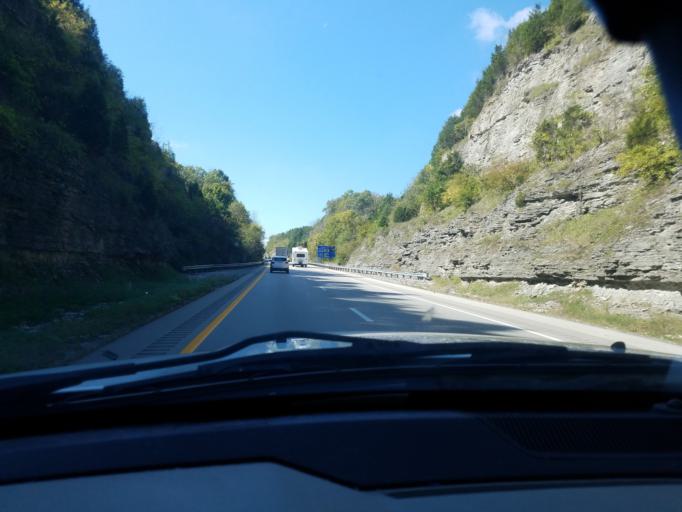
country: US
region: Kentucky
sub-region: Franklin County
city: Frankfort
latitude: 38.1601
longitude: -84.8629
